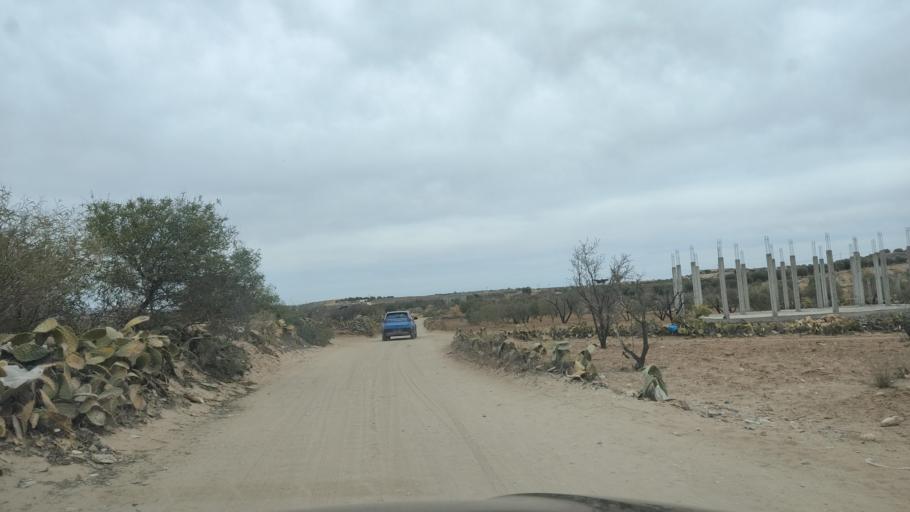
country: TN
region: Al Qasrayn
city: Kasserine
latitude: 35.2311
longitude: 8.9100
